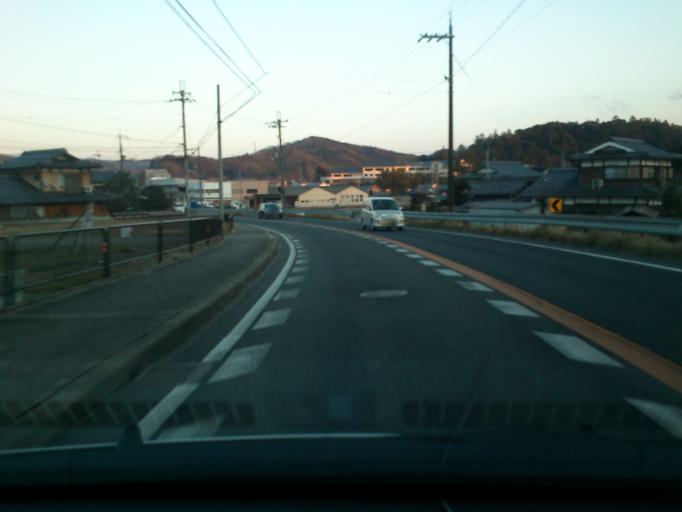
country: JP
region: Kyoto
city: Kameoka
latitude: 35.1125
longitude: 135.4647
